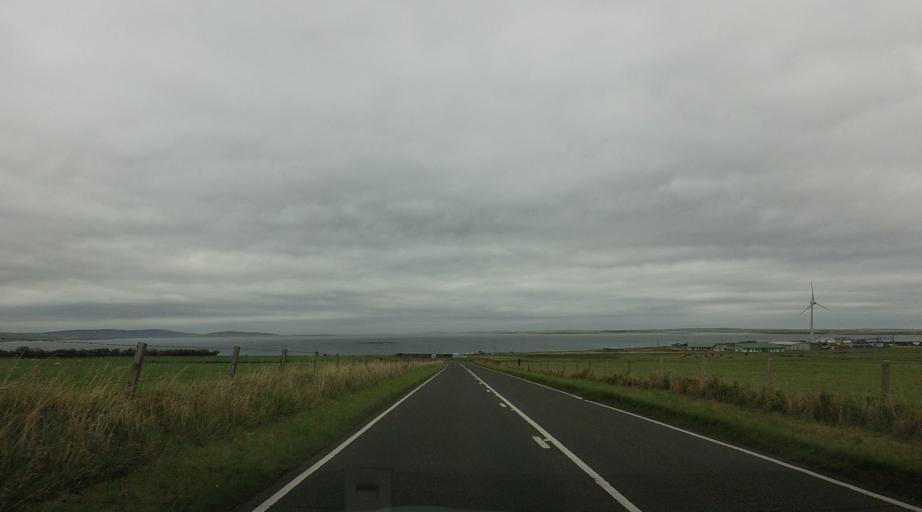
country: GB
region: Scotland
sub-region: Orkney Islands
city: Orkney
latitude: 58.9958
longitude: -2.9935
